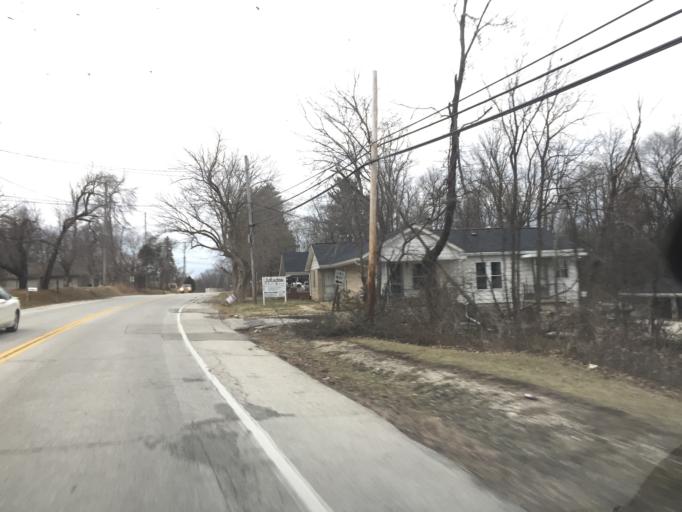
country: US
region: Indiana
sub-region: Monroe County
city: Bloomington
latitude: 39.1823
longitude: -86.5500
